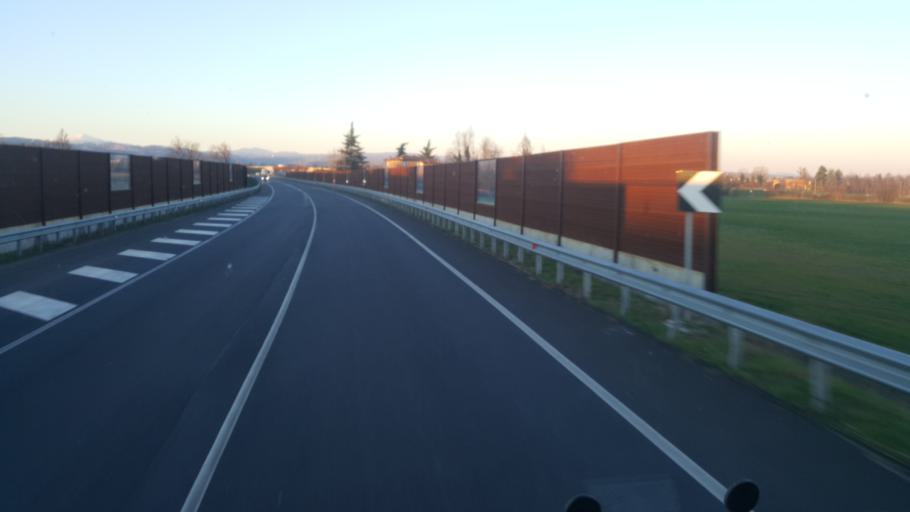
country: IT
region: Emilia-Romagna
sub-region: Provincia di Bologna
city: Bazzano
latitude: 44.5140
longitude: 11.0751
